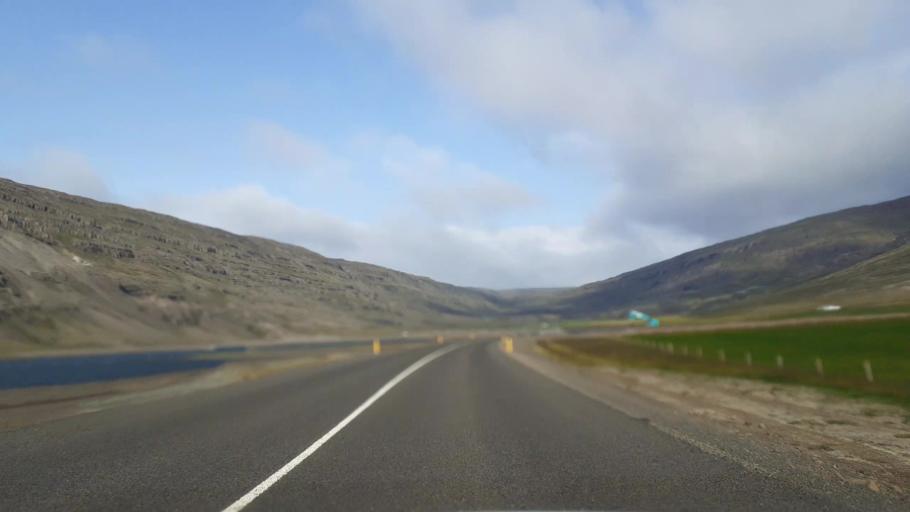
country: IS
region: East
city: Reydarfjoerdur
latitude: 64.7884
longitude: -14.4714
